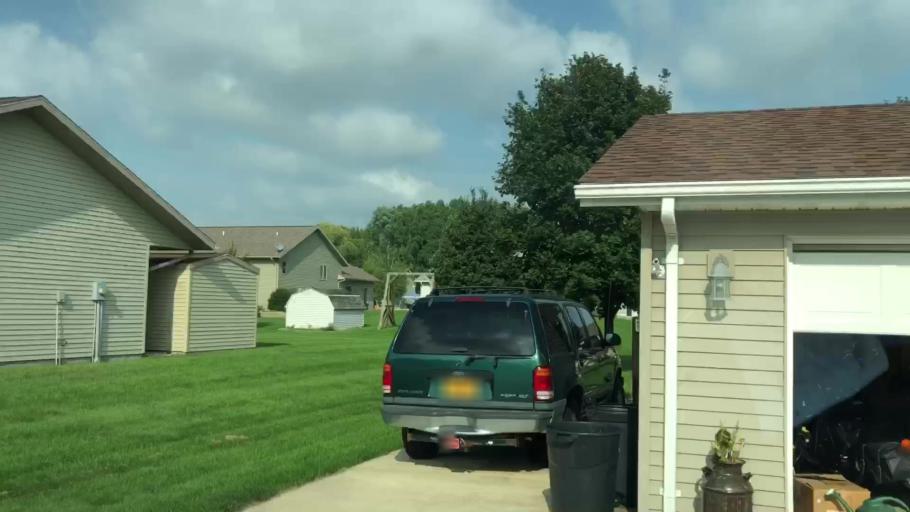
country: US
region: Iowa
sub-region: O'Brien County
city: Sheldon
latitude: 43.1721
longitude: -95.8482
